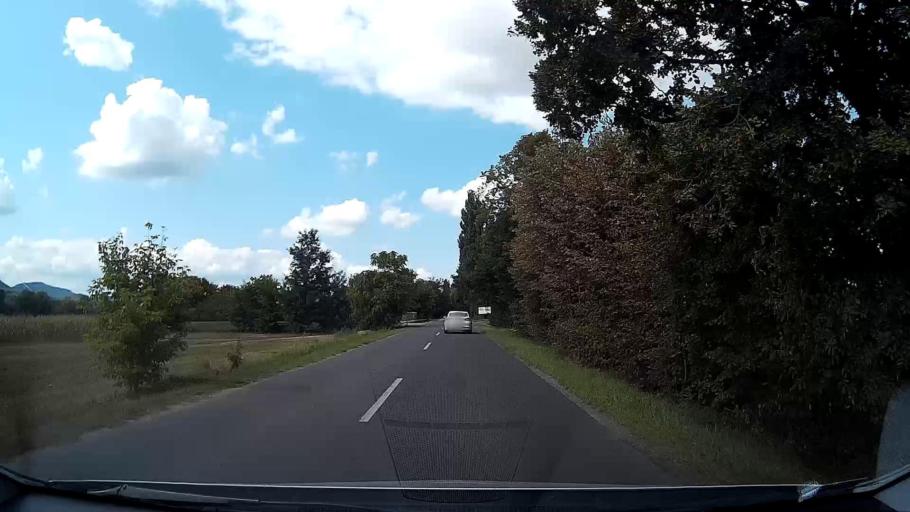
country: HU
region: Pest
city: Tahitotfalu
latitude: 47.7386
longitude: 19.1012
